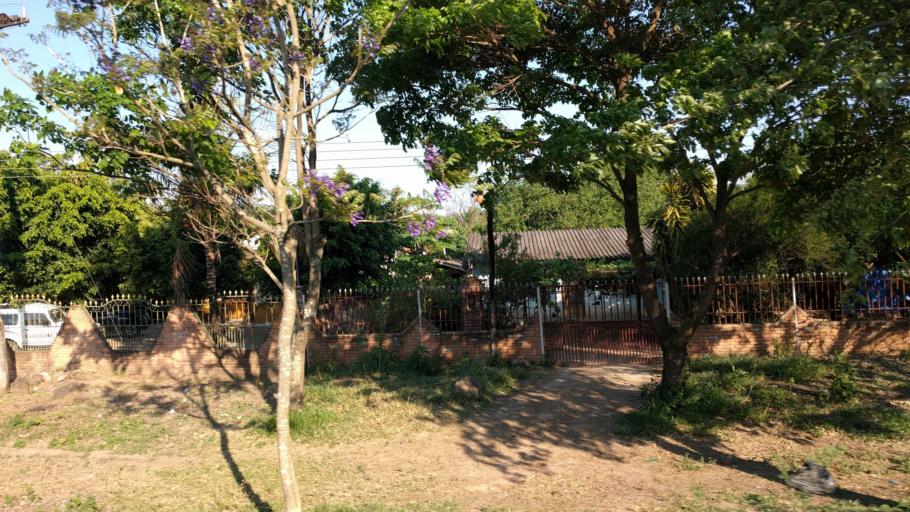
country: BO
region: Santa Cruz
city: Jorochito
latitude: -18.1279
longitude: -63.4672
